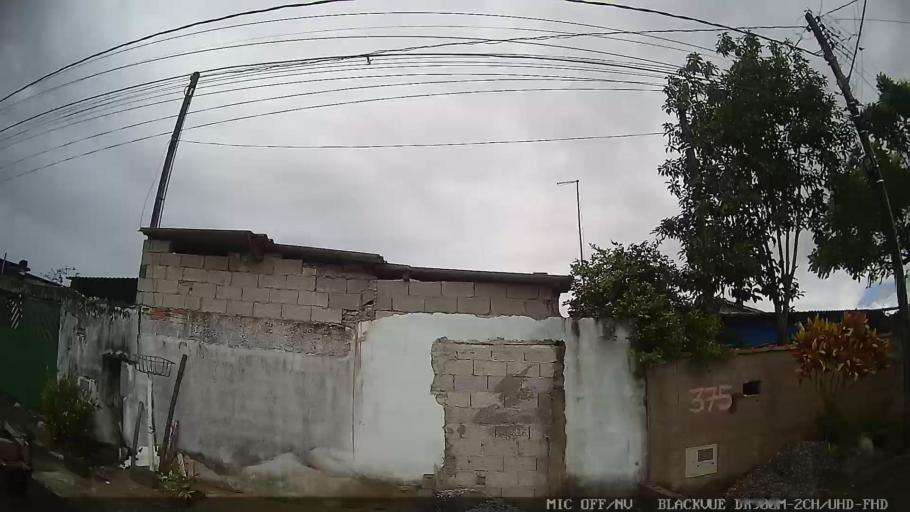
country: BR
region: Sao Paulo
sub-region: Itanhaem
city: Itanhaem
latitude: -24.1598
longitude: -46.7999
